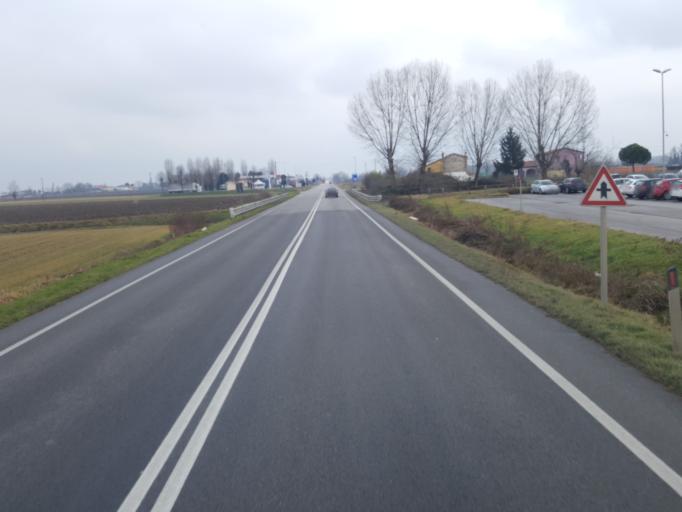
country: IT
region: Veneto
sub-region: Provincia di Padova
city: Pozzonovo
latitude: 45.2095
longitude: 11.7813
